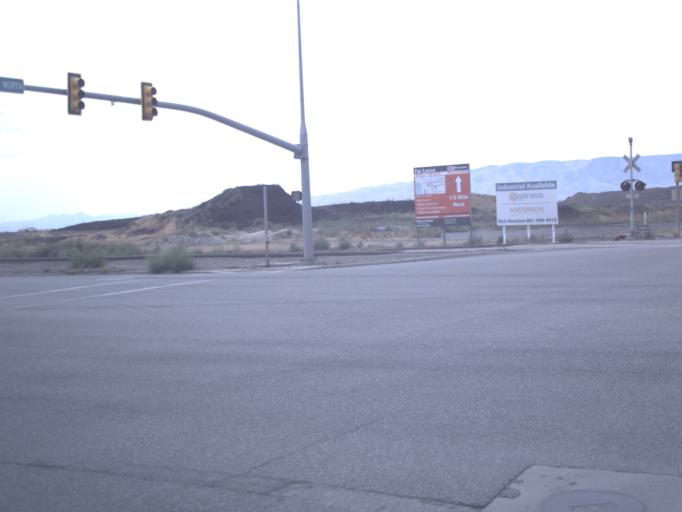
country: US
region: Utah
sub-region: Utah County
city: Lindon
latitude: 40.3263
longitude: -111.7371
